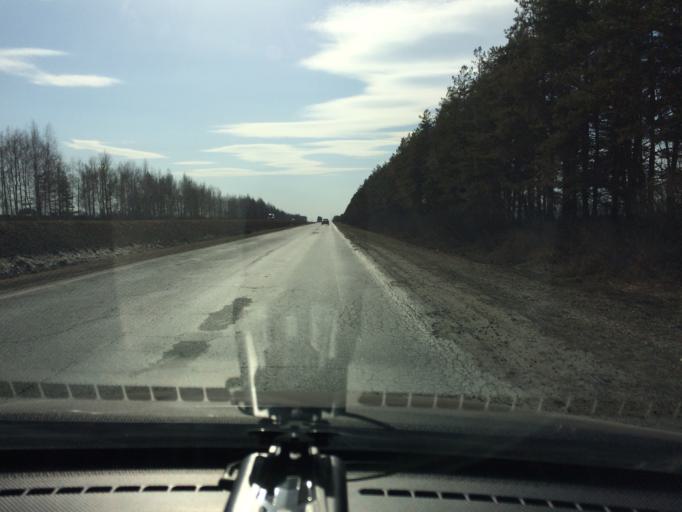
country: RU
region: Mariy-El
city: Yoshkar-Ola
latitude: 56.7259
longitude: 48.1263
